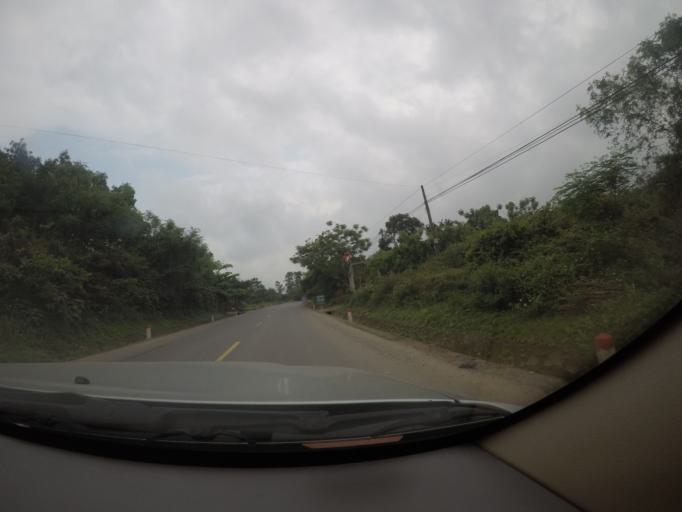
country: VN
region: Quang Binh
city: Kien Giang
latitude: 17.2206
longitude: 106.7088
